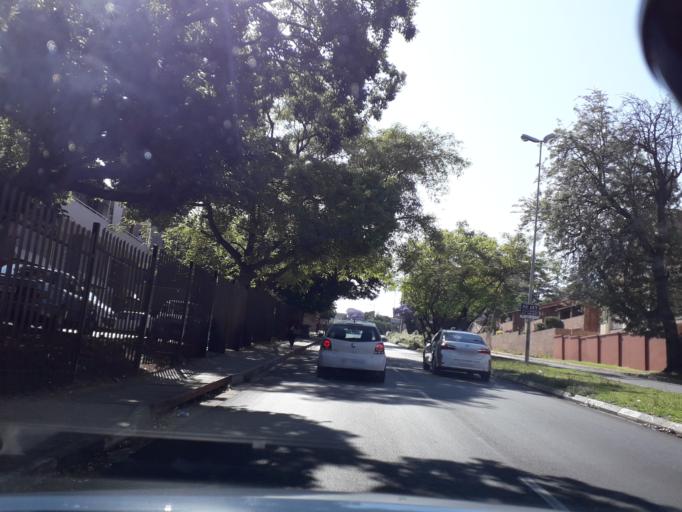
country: ZA
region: Gauteng
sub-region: City of Johannesburg Metropolitan Municipality
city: Johannesburg
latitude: -26.0921
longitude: 27.9970
